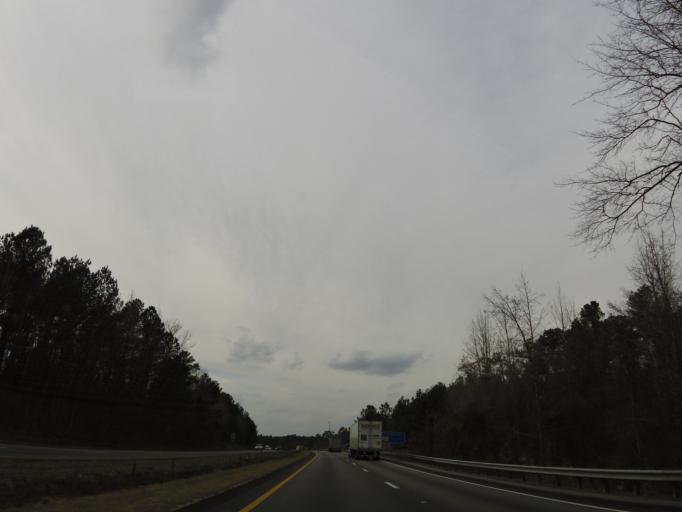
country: US
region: South Carolina
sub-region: Calhoun County
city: Oak Grove
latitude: 33.7611
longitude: -80.9551
